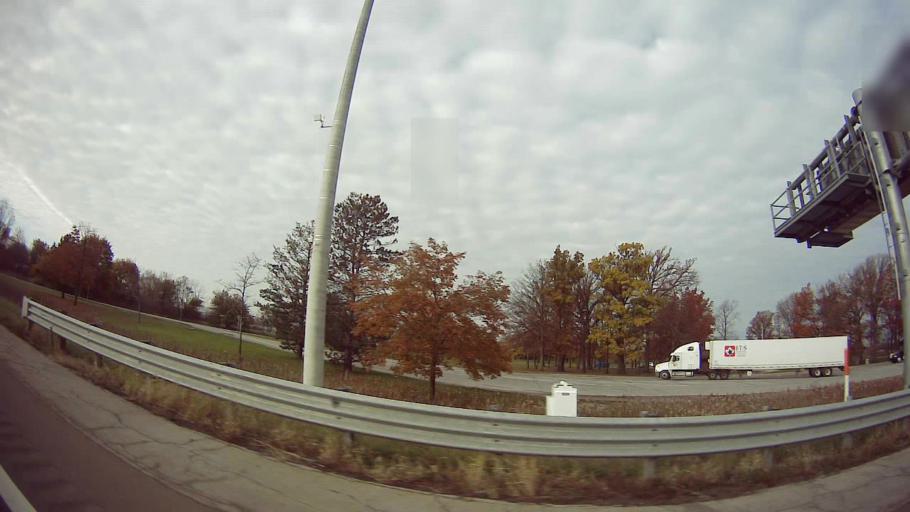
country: US
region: Michigan
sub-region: Monroe County
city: Carleton
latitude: 42.0426
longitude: -83.3541
